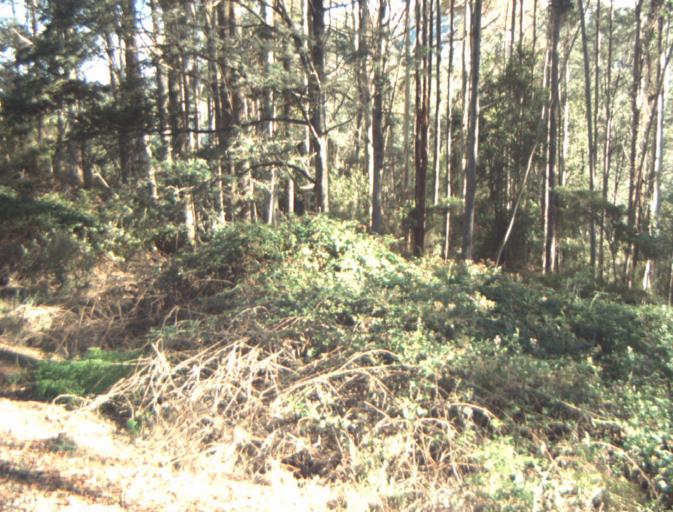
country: AU
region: Tasmania
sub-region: Launceston
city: Mayfield
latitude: -41.2943
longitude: 147.1978
